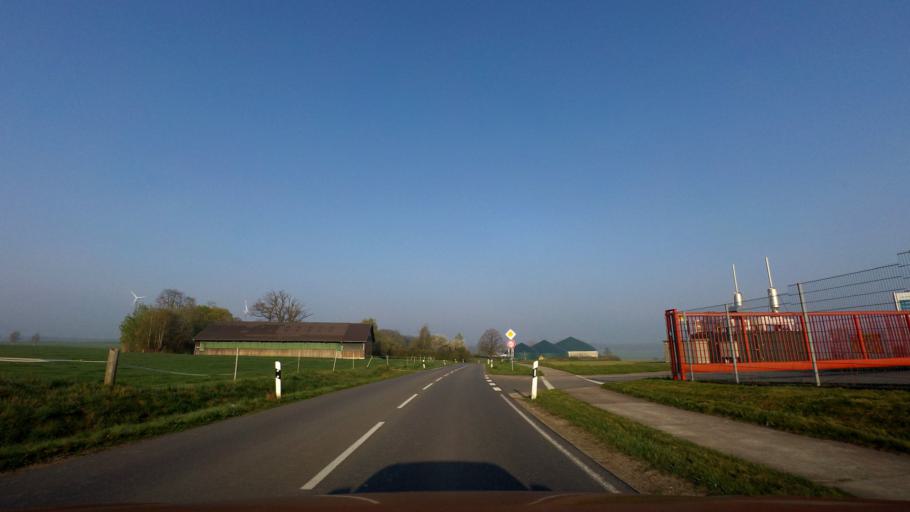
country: DE
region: Lower Saxony
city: Neuenkirchen
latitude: 52.1826
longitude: 8.4017
